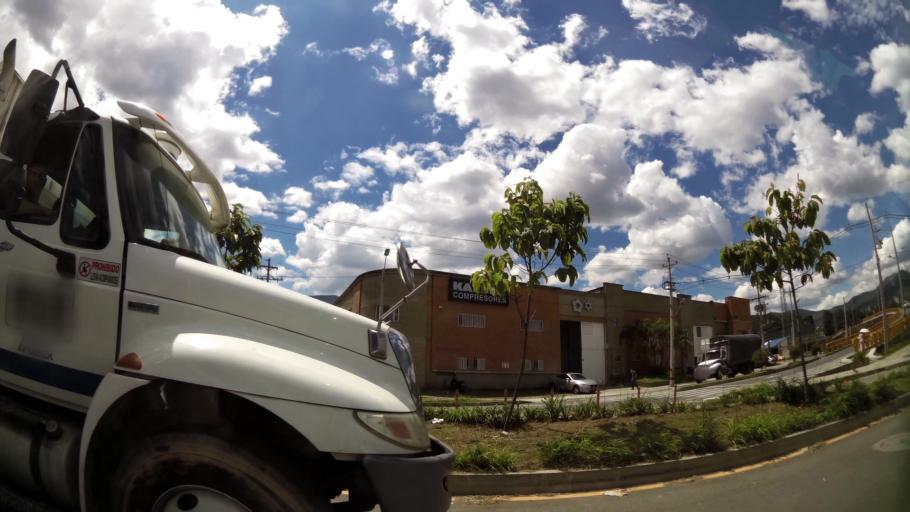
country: CO
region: Antioquia
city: Sabaneta
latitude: 6.1516
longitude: -75.6252
